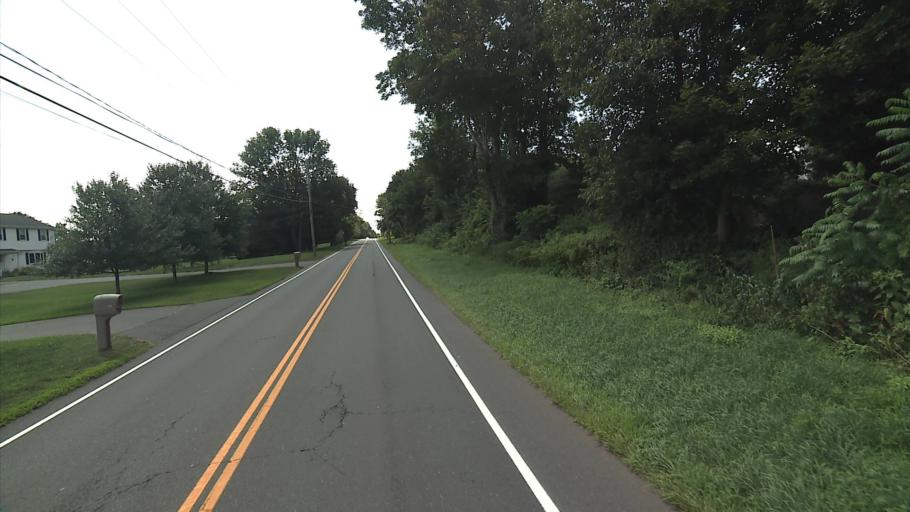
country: US
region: Connecticut
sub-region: Tolland County
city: Ellington
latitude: 41.8835
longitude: -72.4828
